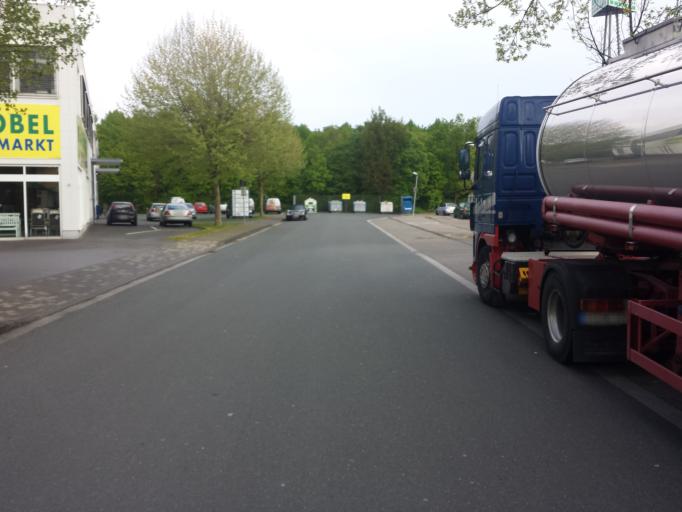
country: DE
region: North Rhine-Westphalia
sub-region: Regierungsbezirk Detmold
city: Guetersloh
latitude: 51.8896
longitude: 8.3609
